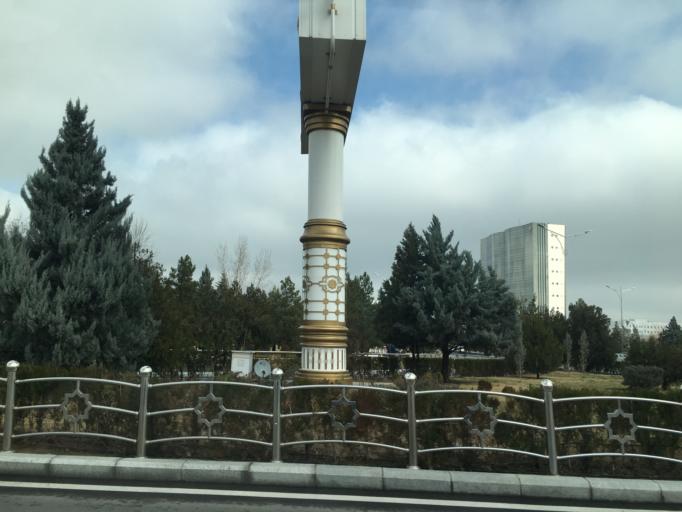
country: TM
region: Ahal
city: Ashgabat
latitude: 37.9253
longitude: 58.3761
